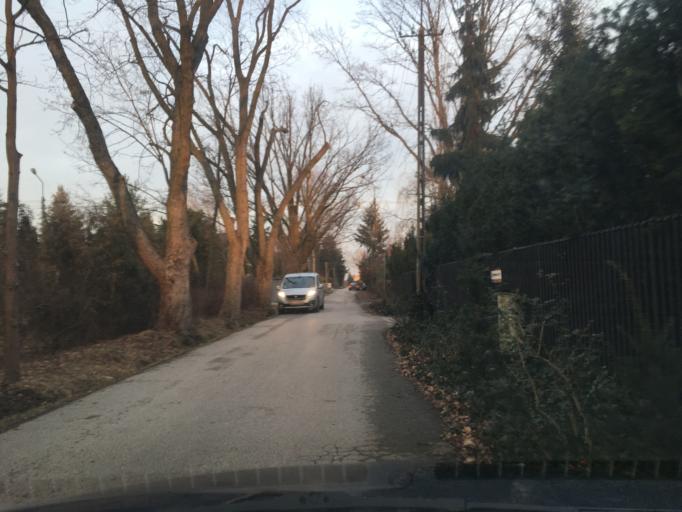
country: PL
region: Masovian Voivodeship
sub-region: Powiat piaseczynski
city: Lesznowola
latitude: 52.0363
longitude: 20.9589
